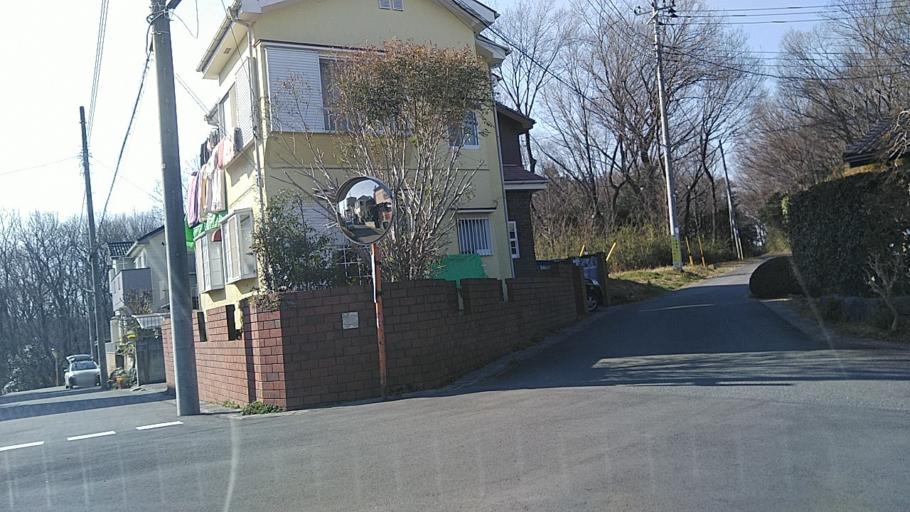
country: JP
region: Saitama
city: Fukiage-fujimi
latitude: 36.0775
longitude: 139.4010
